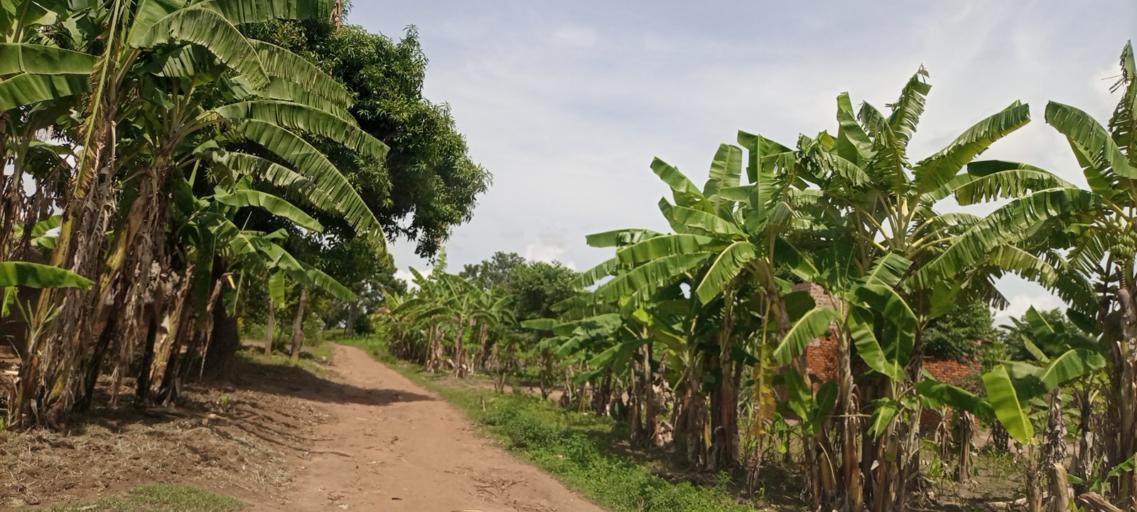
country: UG
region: Eastern Region
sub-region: Budaka District
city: Budaka
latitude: 1.1697
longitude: 33.9449
